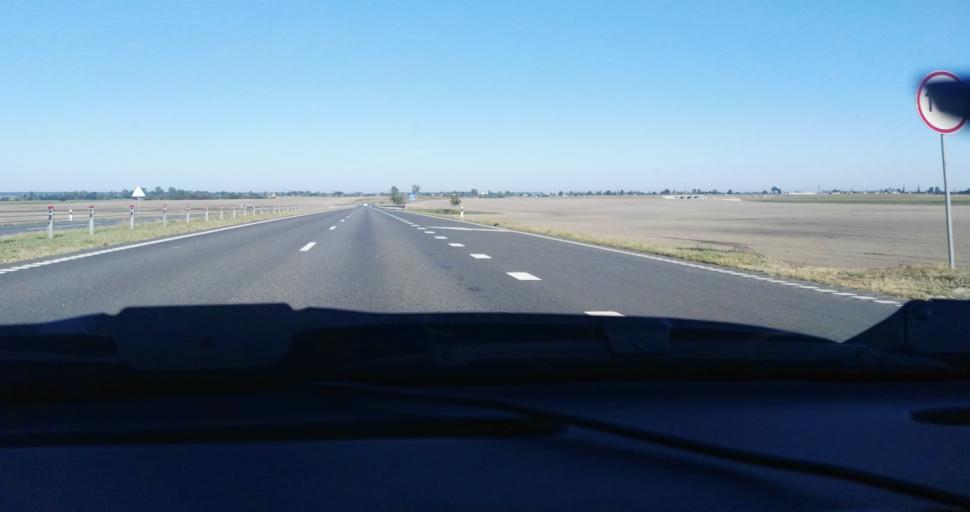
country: BY
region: Gomel
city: Buda-Kashalyova
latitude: 52.5053
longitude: 30.6443
